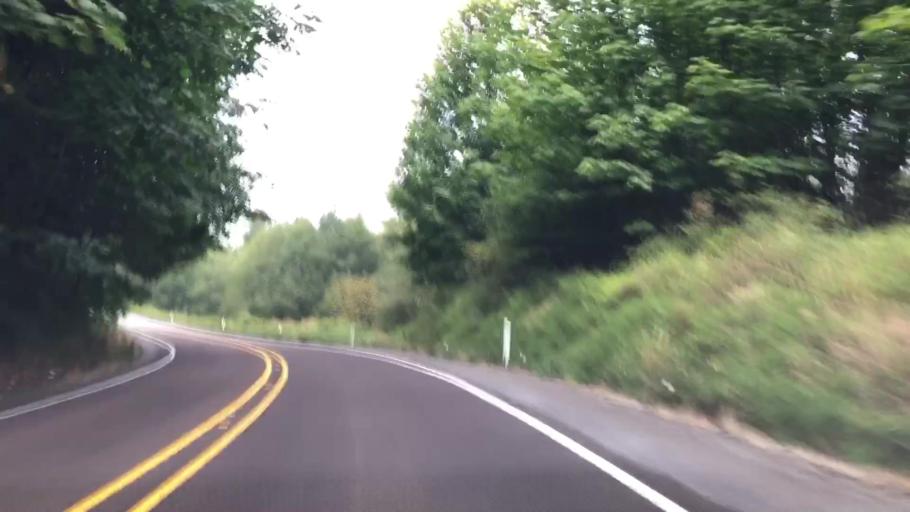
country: US
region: Washington
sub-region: Kitsap County
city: Navy Yard City
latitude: 47.5273
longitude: -122.7303
